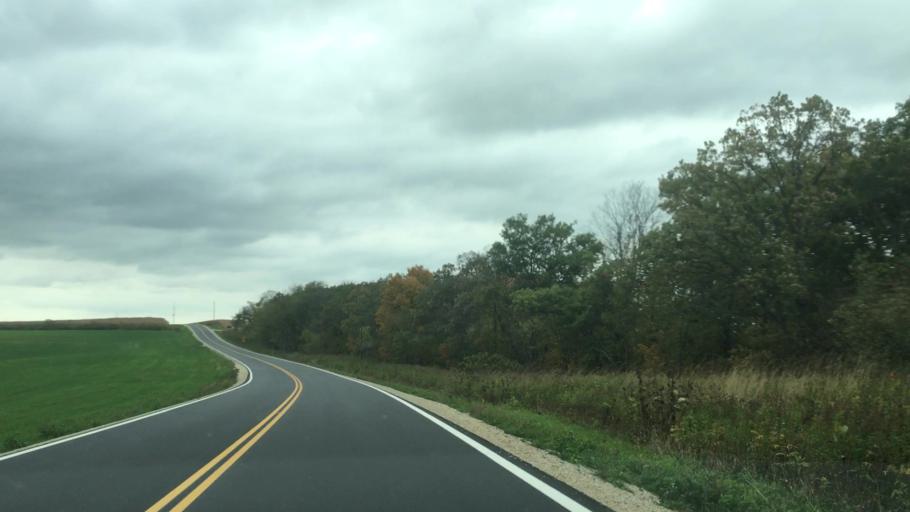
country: US
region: Minnesota
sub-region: Fillmore County
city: Preston
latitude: 43.7599
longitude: -92.0102
